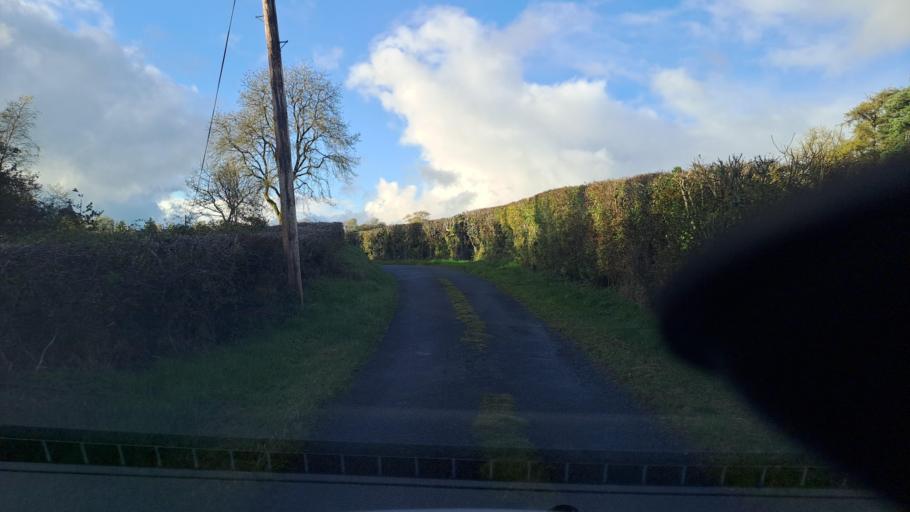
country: IE
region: Ulster
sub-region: An Cabhan
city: Bailieborough
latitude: 53.9324
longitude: -6.9413
